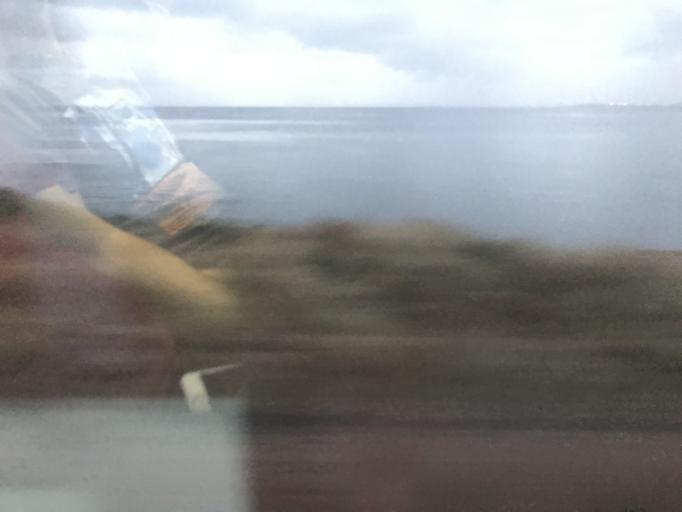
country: TR
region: Kocaeli
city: Tavsancil
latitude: 40.7723
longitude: 29.5550
